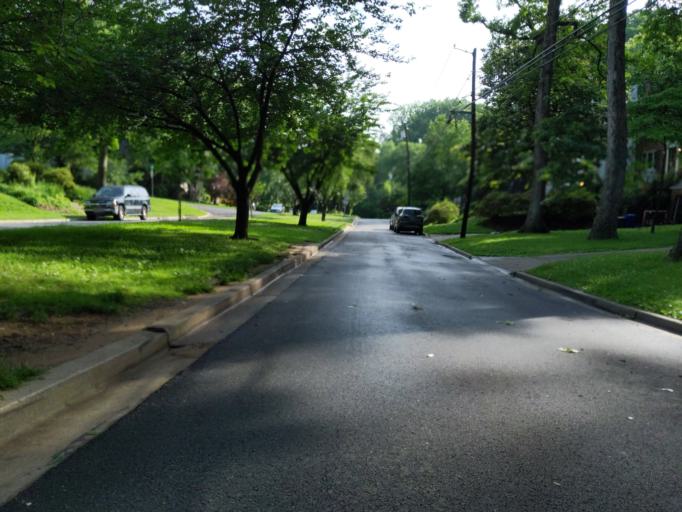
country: US
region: Maryland
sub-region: Montgomery County
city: Forest Glen
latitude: 39.0104
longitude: -77.0364
